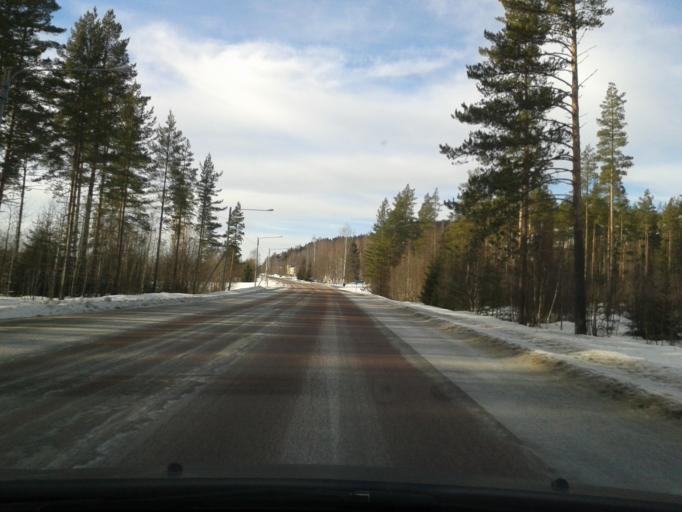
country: SE
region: Vaesternorrland
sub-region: OErnskoeldsviks Kommun
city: Bjasta
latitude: 63.3804
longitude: 18.4149
